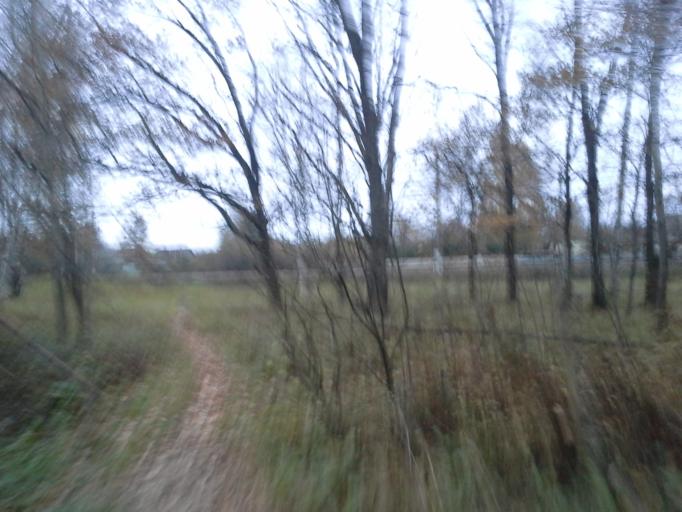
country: RU
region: Moskovskaya
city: Zhavoronki
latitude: 55.6413
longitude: 37.1118
